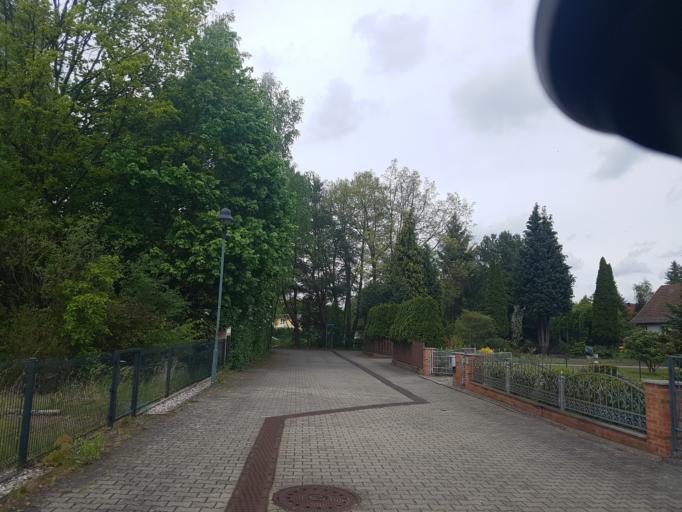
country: DE
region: Brandenburg
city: Tschernitz
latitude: 51.6207
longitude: 14.5969
